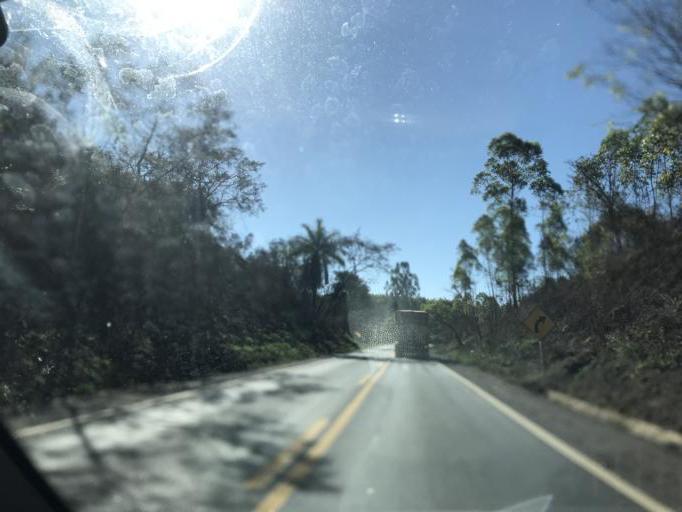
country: BR
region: Minas Gerais
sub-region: Bambui
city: Bambui
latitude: -19.8722
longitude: -45.9859
